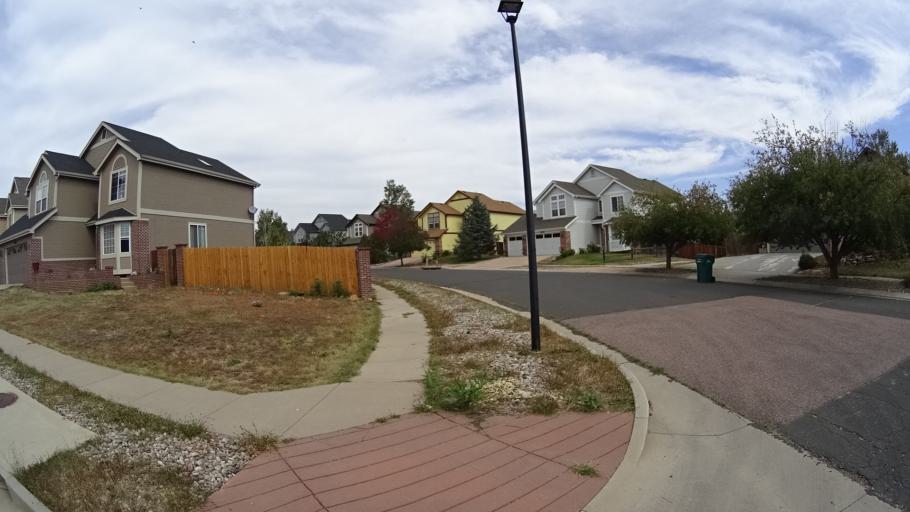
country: US
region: Colorado
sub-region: El Paso County
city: Cimarron Hills
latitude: 38.8992
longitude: -104.7076
